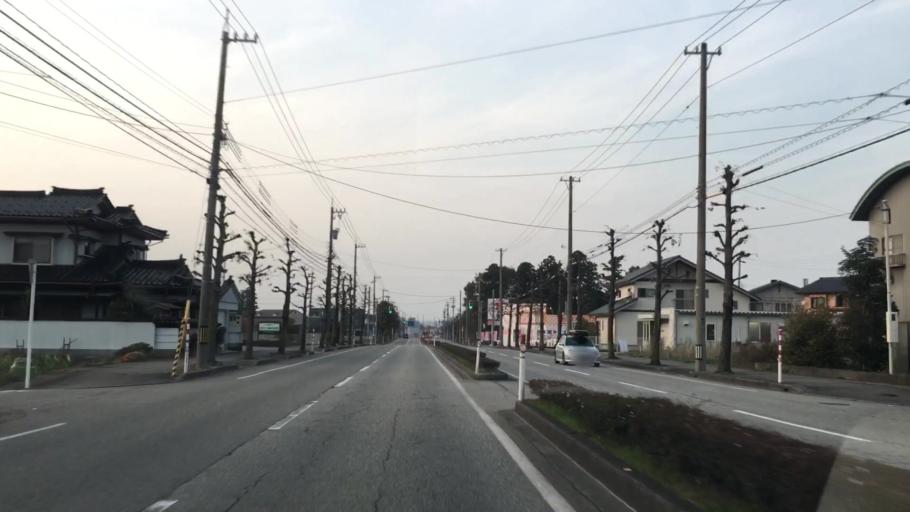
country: JP
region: Toyama
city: Toyama-shi
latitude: 36.6527
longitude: 137.2321
